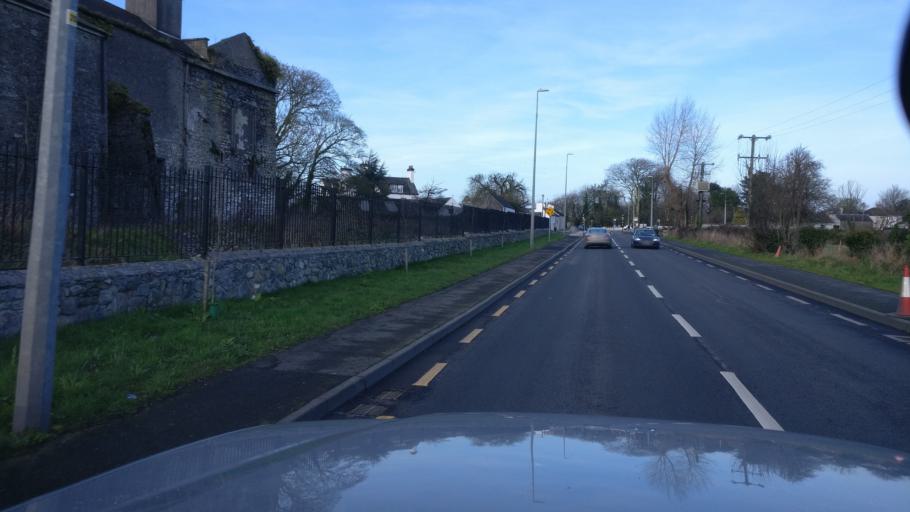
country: IE
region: Leinster
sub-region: Laois
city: Mountmellick
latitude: 53.1098
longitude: -7.3287
